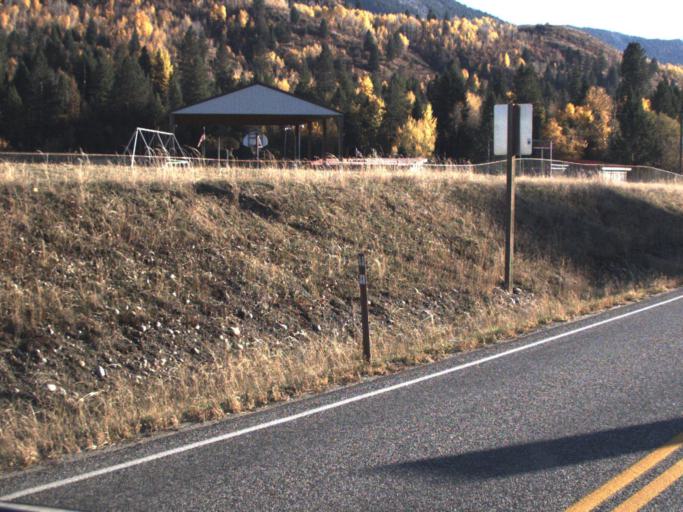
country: CA
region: British Columbia
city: Rossland
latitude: 48.9117
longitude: -117.7908
